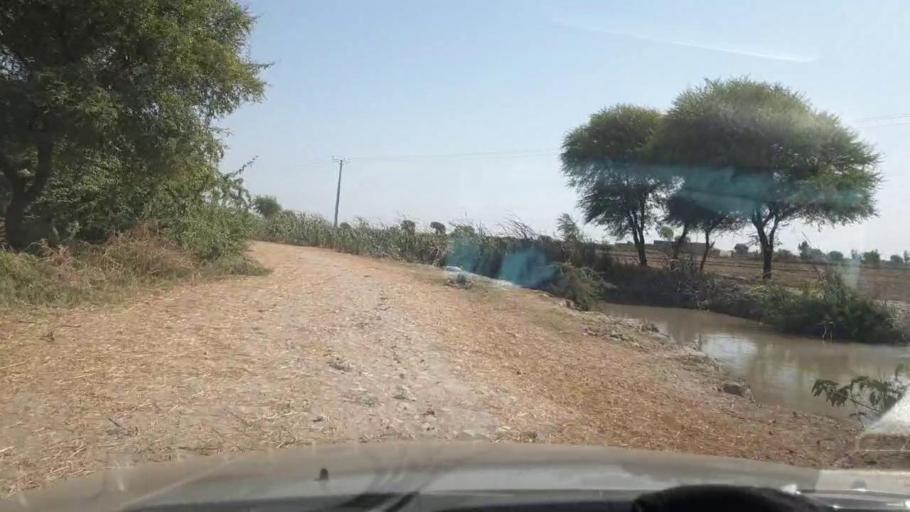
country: PK
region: Sindh
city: Daro Mehar
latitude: 24.9696
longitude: 68.1176
